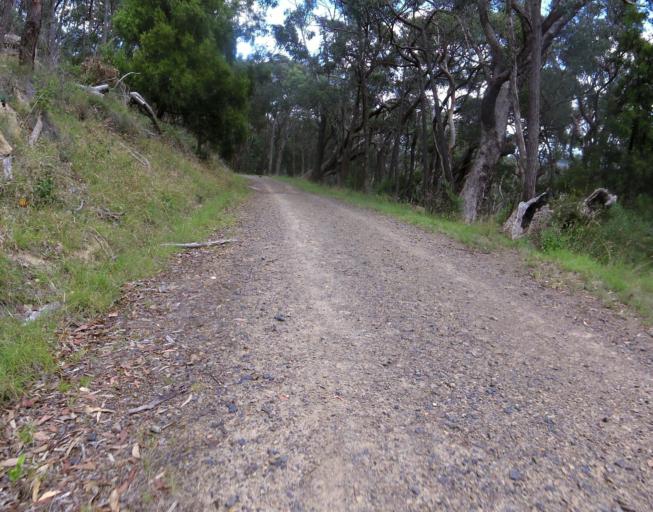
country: AU
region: Victoria
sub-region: Yarra Ranges
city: Montrose
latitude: -37.8256
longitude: 145.3443
